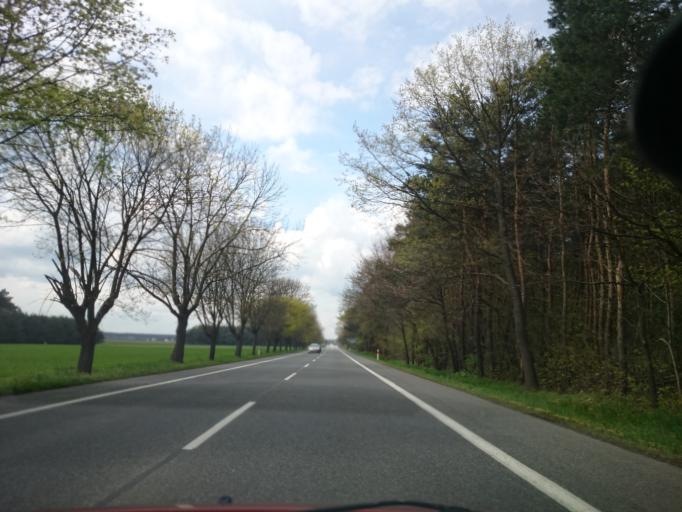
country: PL
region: Opole Voivodeship
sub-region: Powiat strzelecki
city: Izbicko
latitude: 50.5746
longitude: 18.1413
